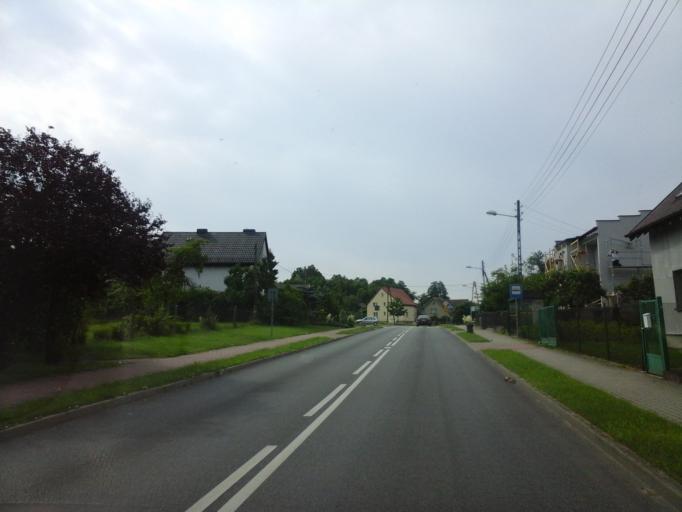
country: PL
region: West Pomeranian Voivodeship
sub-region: Powiat choszczenski
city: Recz
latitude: 53.2545
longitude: 15.5414
